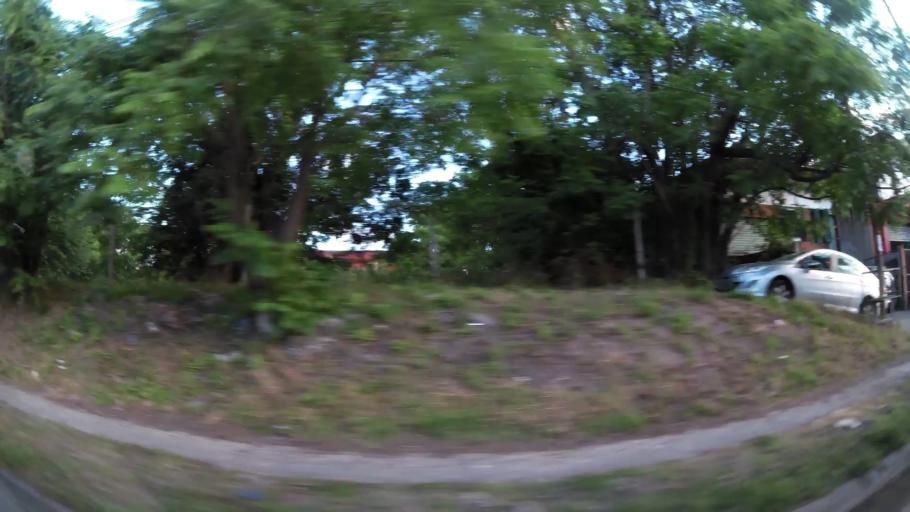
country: AR
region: Buenos Aires
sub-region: Partido de Tigre
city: Tigre
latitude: -34.4691
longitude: -58.5617
